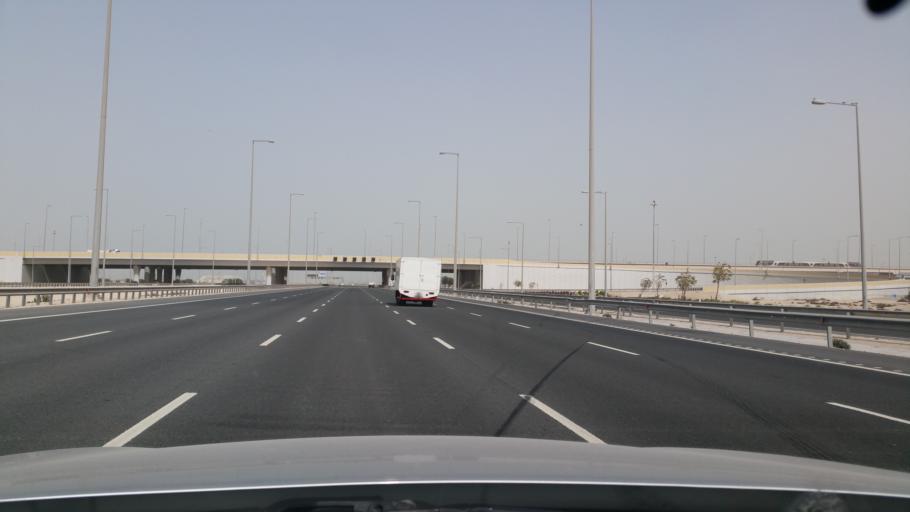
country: QA
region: Al Wakrah
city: Al Wakrah
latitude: 25.2185
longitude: 51.5791
